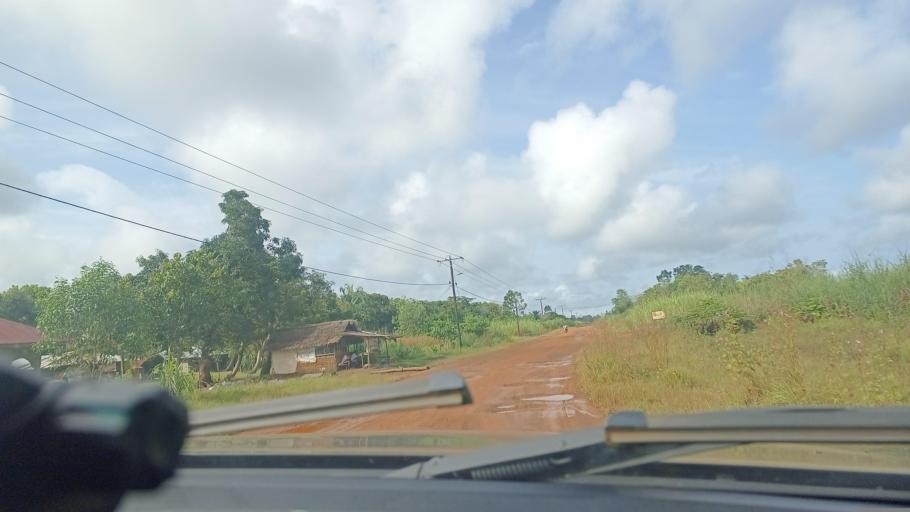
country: LR
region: Grand Cape Mount
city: Robertsport
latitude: 6.6946
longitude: -11.1052
